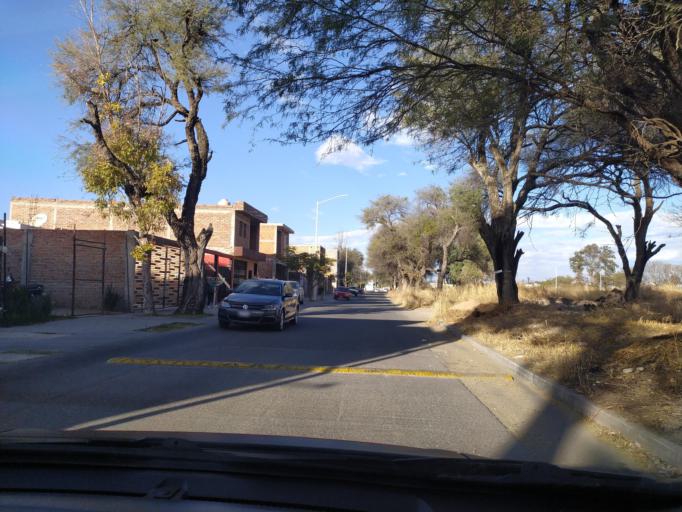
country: MX
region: Guanajuato
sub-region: Purisima del Rincon
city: Monte Grande
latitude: 21.0062
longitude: -101.8717
